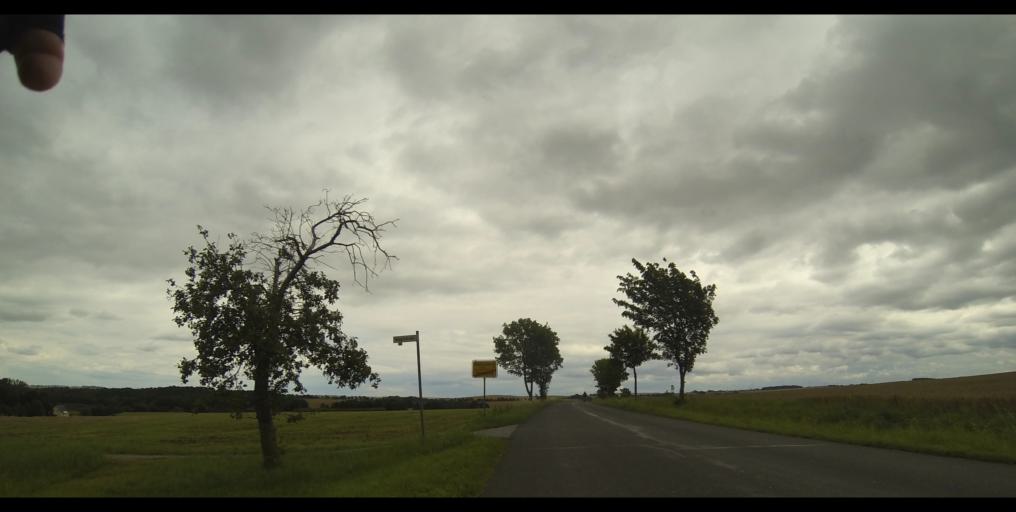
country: DE
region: Saxony
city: Reinsberg
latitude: 51.0401
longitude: 13.3644
